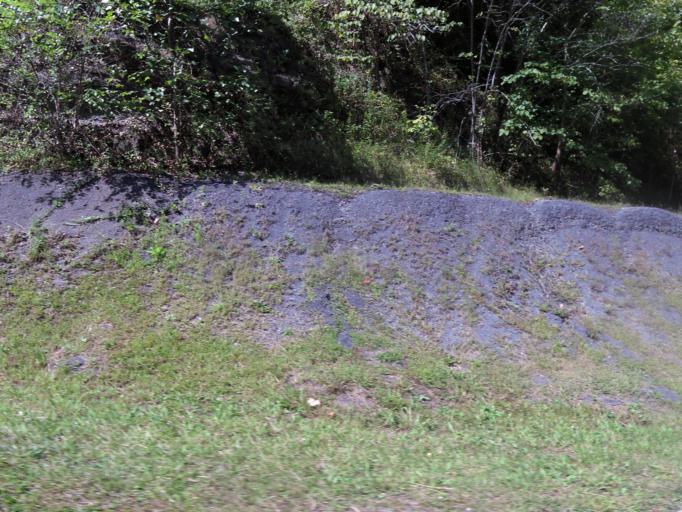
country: US
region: Kentucky
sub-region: Leslie County
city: Hyden
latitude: 37.1570
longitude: -83.3709
